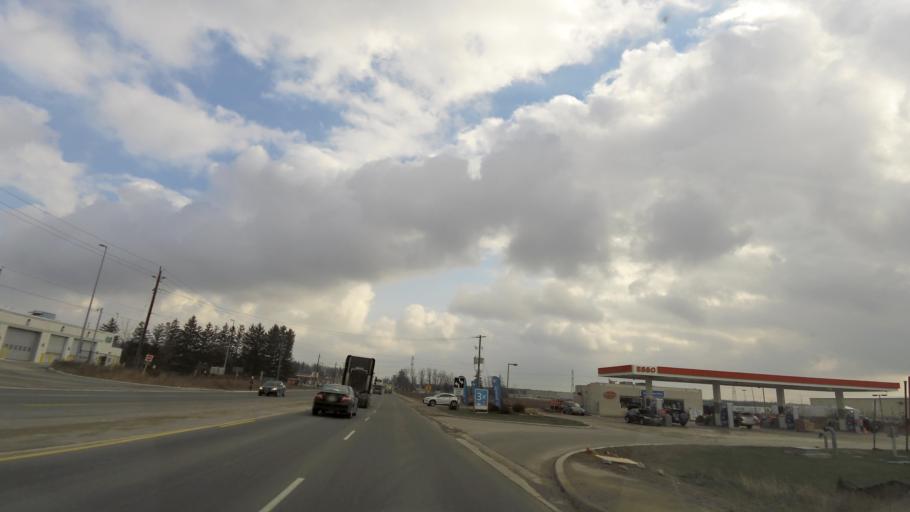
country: CA
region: Ontario
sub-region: Wellington County
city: Guelph
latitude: 43.4601
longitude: -80.1343
